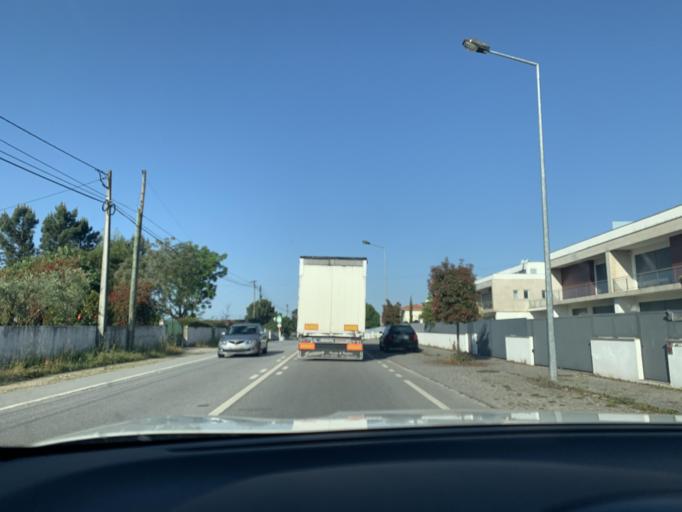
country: PT
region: Viseu
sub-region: Viseu
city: Viseu
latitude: 40.6248
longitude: -7.8904
